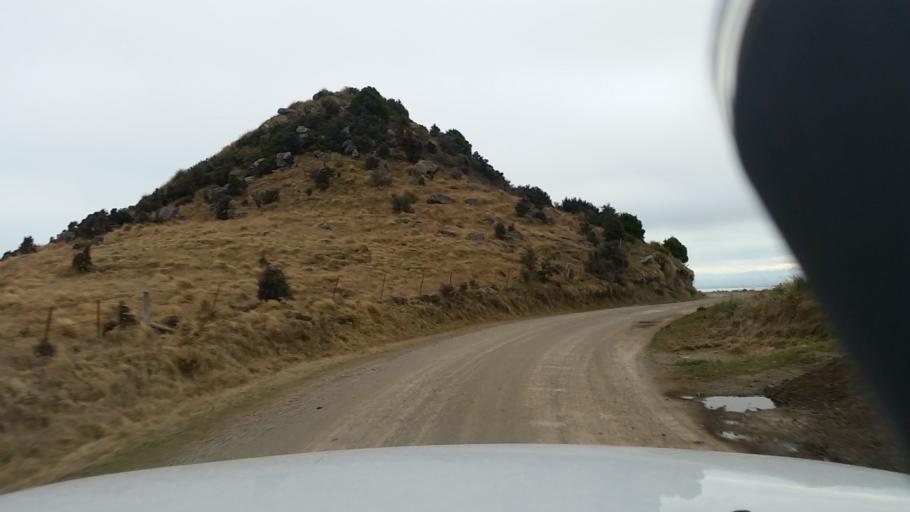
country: NZ
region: Canterbury
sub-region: Christchurch City
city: Christchurch
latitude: -43.8132
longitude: 172.8112
